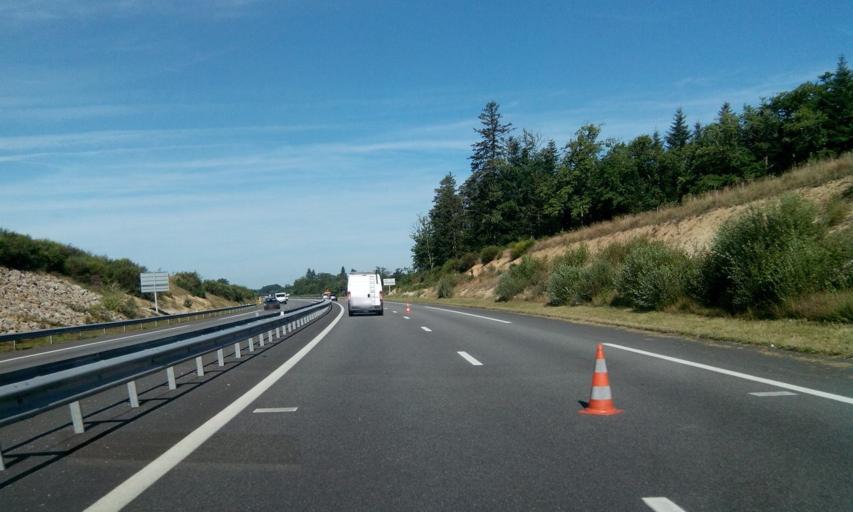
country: FR
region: Limousin
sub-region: Departement de la Haute-Vienne
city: Veyrac
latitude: 45.8869
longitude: 1.0746
